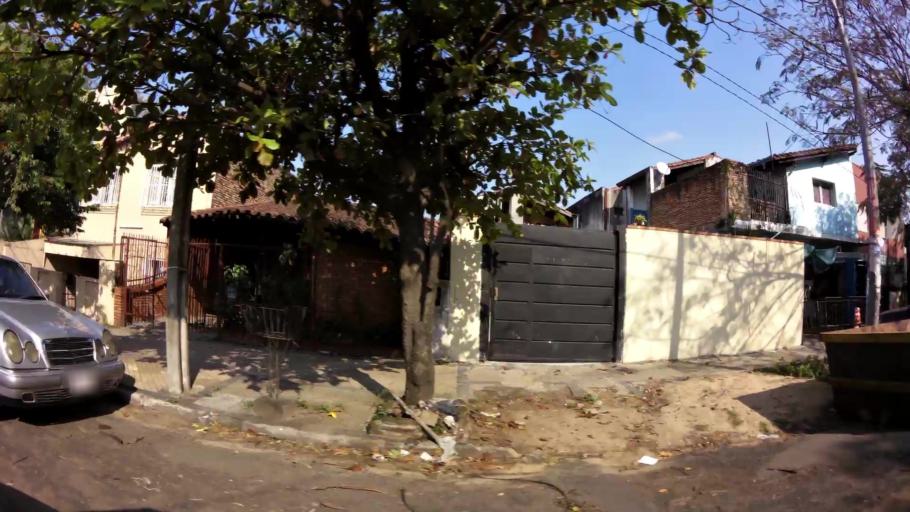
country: PY
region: Asuncion
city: Asuncion
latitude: -25.3014
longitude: -57.6280
